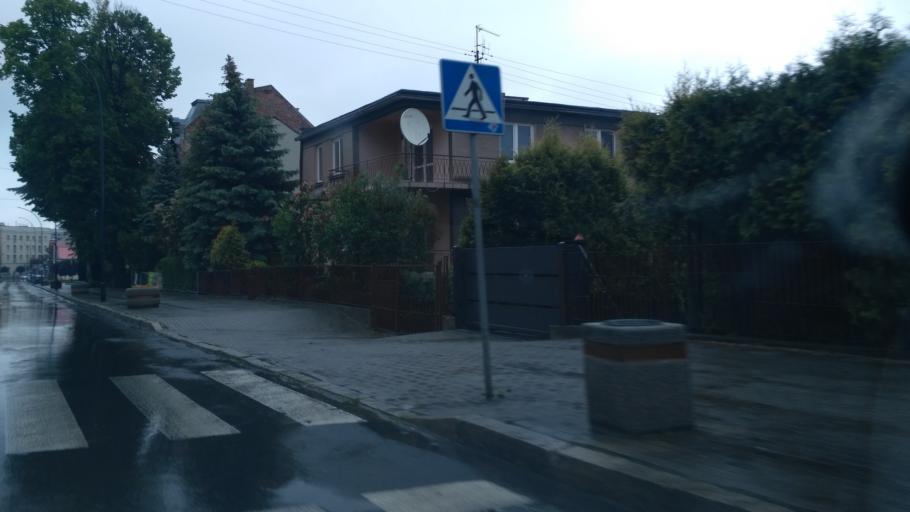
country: PL
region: Subcarpathian Voivodeship
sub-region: Powiat jasielski
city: Jaslo
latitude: 49.7406
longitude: 21.4679
